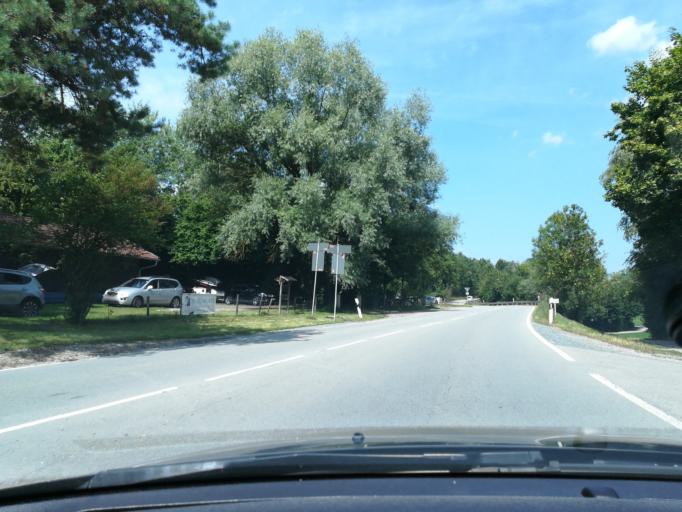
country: DE
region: Bavaria
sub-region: Upper Bavaria
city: Grafing bei Munchen
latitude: 48.0374
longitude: 11.9456
